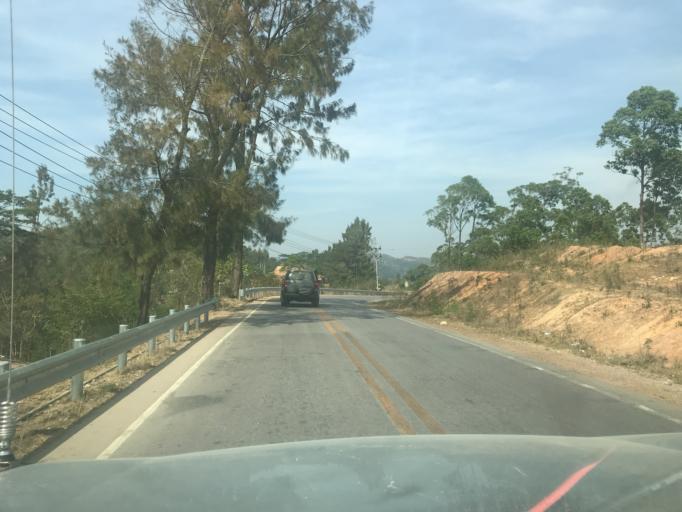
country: TL
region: Aileu
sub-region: Aileu Villa
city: Aileu
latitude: -8.6829
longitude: 125.5497
